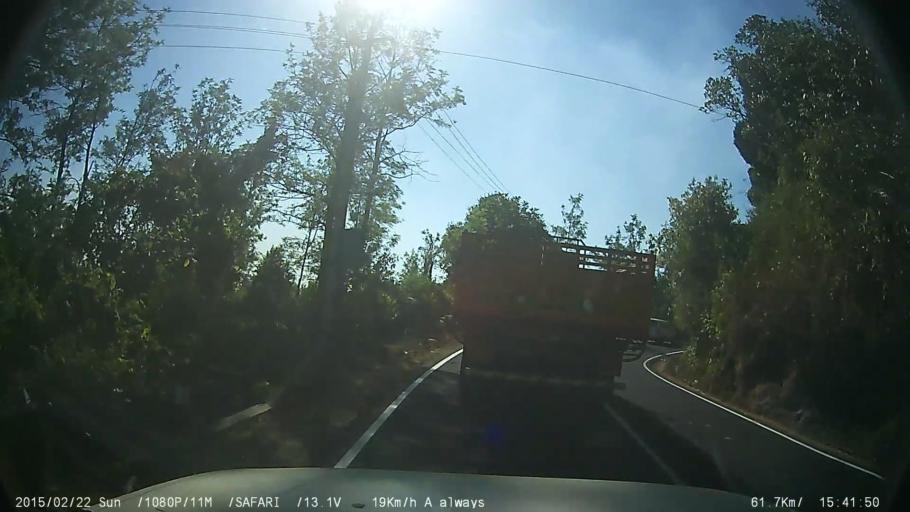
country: IN
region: Kerala
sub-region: Kottayam
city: Erattupetta
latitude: 9.5752
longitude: 76.9746
